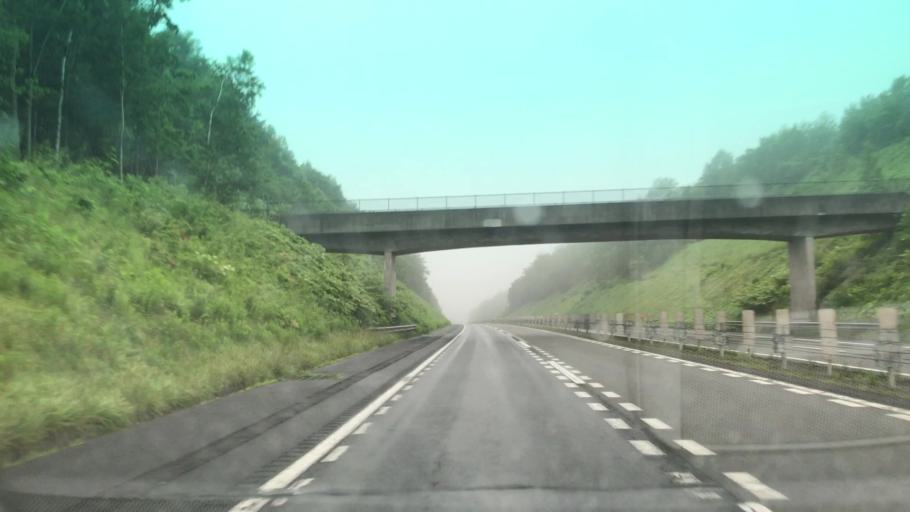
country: JP
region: Hokkaido
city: Tomakomai
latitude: 42.6479
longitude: 141.5360
